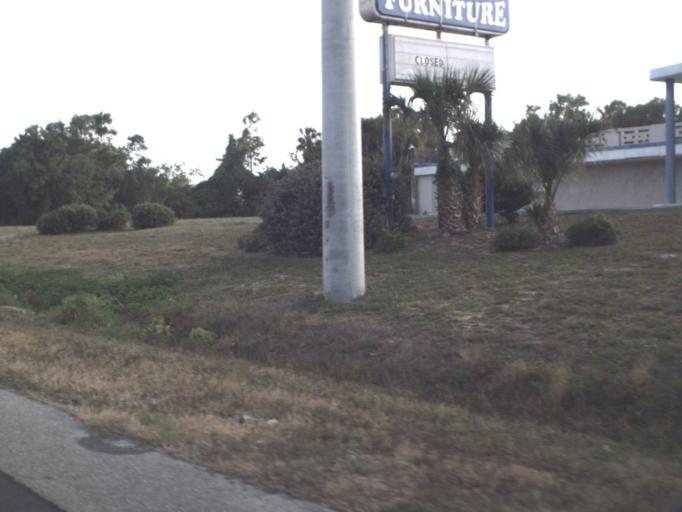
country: US
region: Florida
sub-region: Brevard County
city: Sharpes
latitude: 28.4125
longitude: -80.7552
